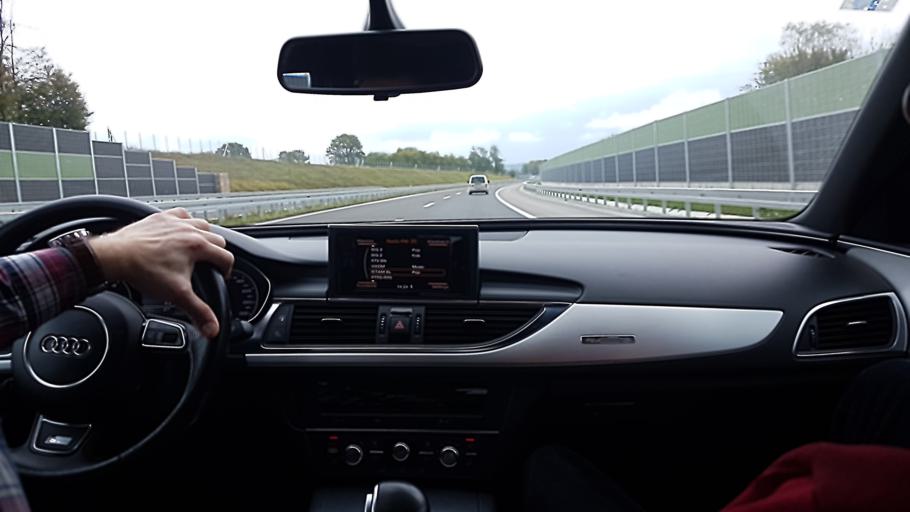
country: BA
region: Republika Srpska
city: Prnjavor
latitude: 44.8476
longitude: 17.7625
